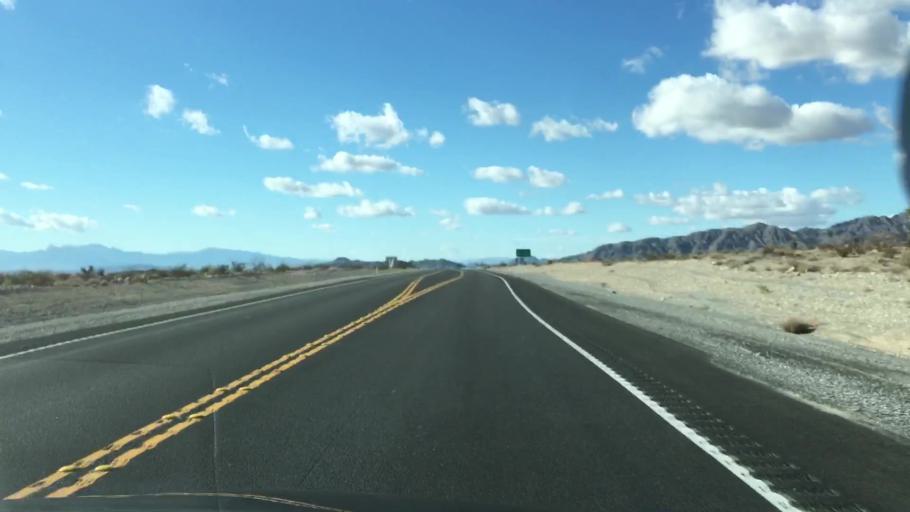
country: US
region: Nevada
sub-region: Nye County
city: Pahrump
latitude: 36.5642
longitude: -116.1189
